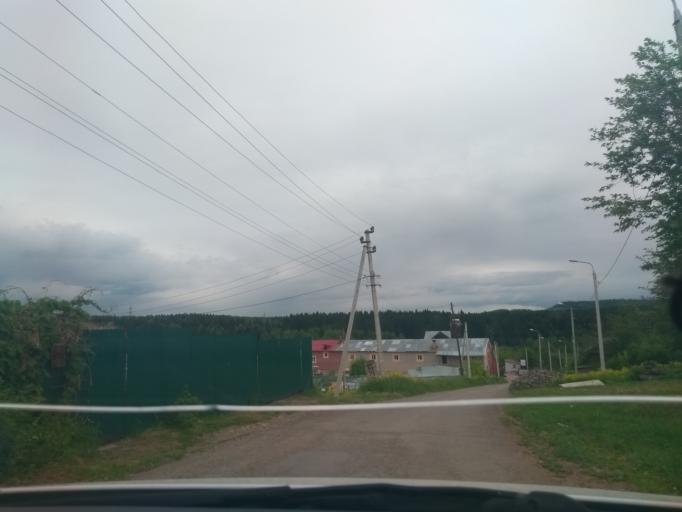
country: RU
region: Perm
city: Perm
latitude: 57.9923
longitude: 56.3377
